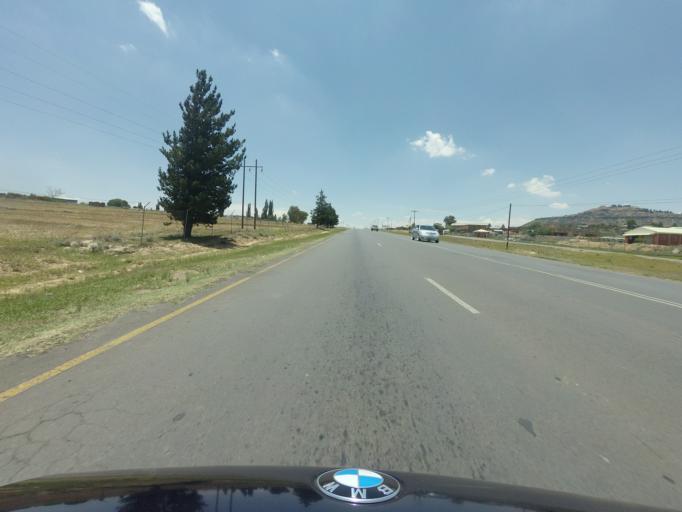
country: LS
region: Maseru
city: Maseru
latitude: -29.2642
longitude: 27.5644
